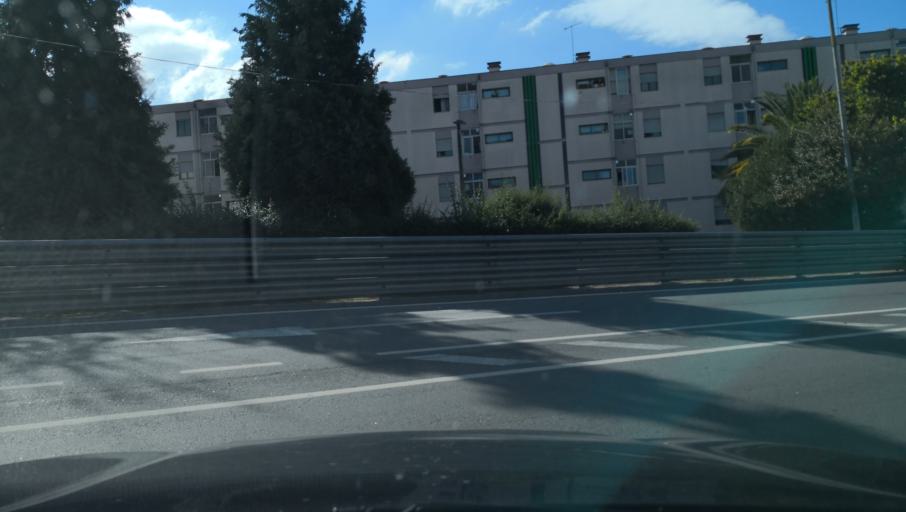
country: PT
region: Vila Real
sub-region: Vila Real
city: Vila Real
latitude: 41.2945
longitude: -7.7299
